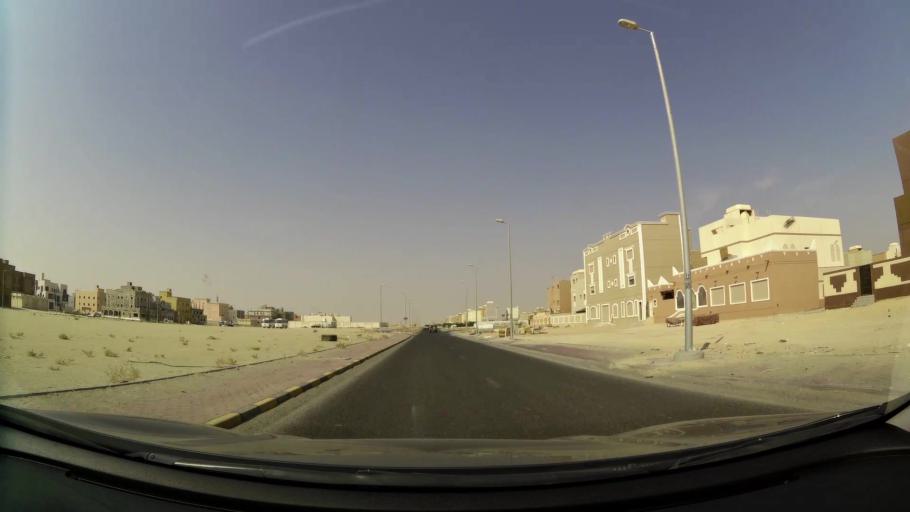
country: KW
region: Al Ahmadi
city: Al Wafrah
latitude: 28.8007
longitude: 48.0533
